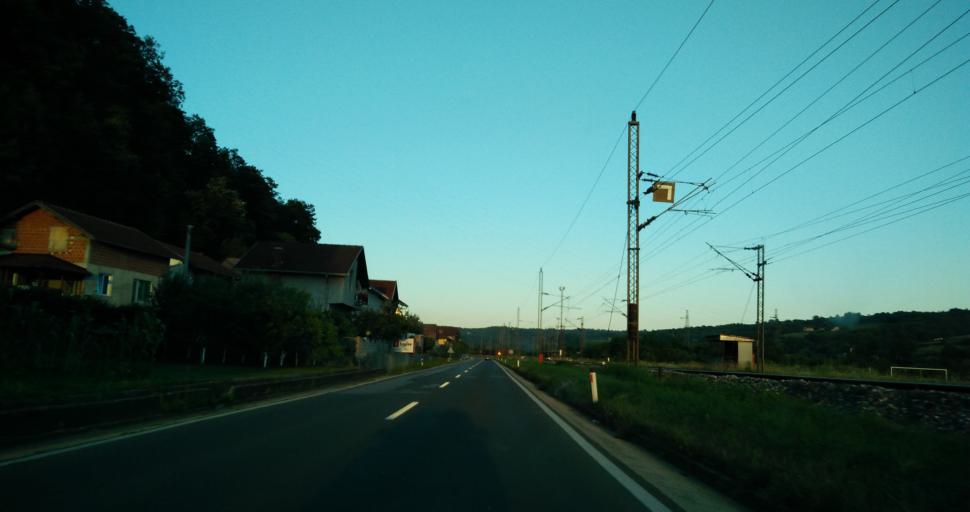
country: BA
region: Republika Srpska
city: Bosanski Novi
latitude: 45.0456
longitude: 16.3956
